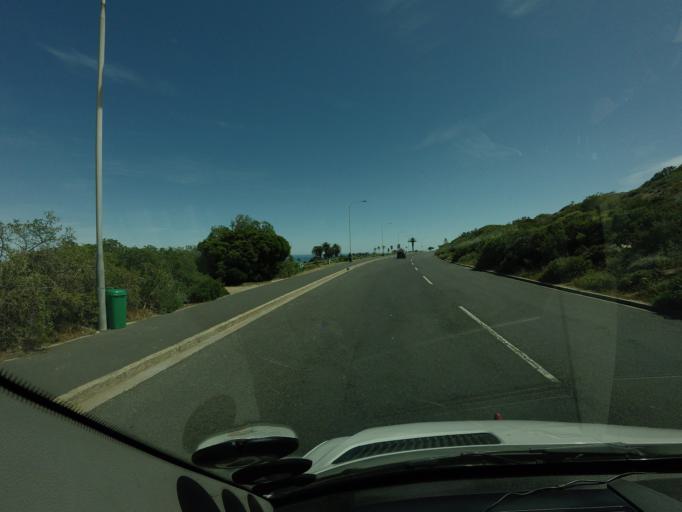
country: ZA
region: Western Cape
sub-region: City of Cape Town
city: Cape Town
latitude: -33.9423
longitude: 18.3754
